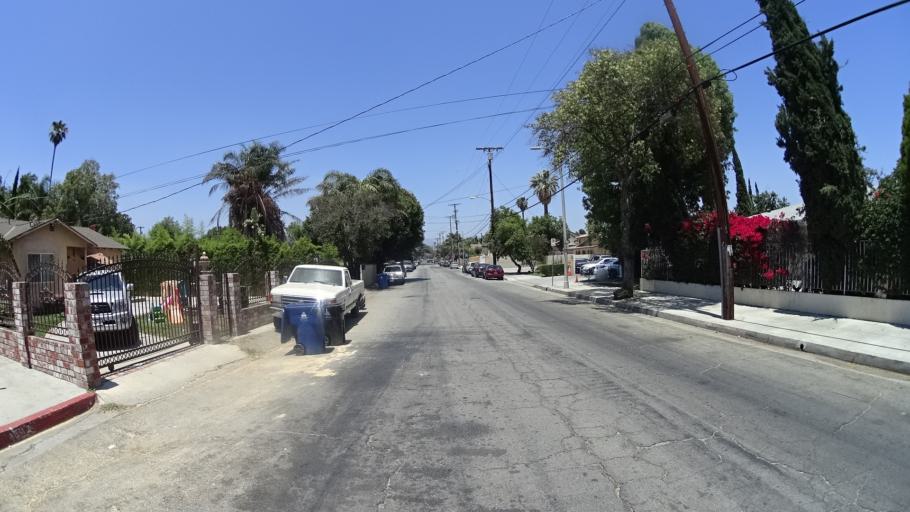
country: US
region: California
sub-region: Los Angeles County
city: Van Nuys
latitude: 34.2221
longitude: -118.4575
